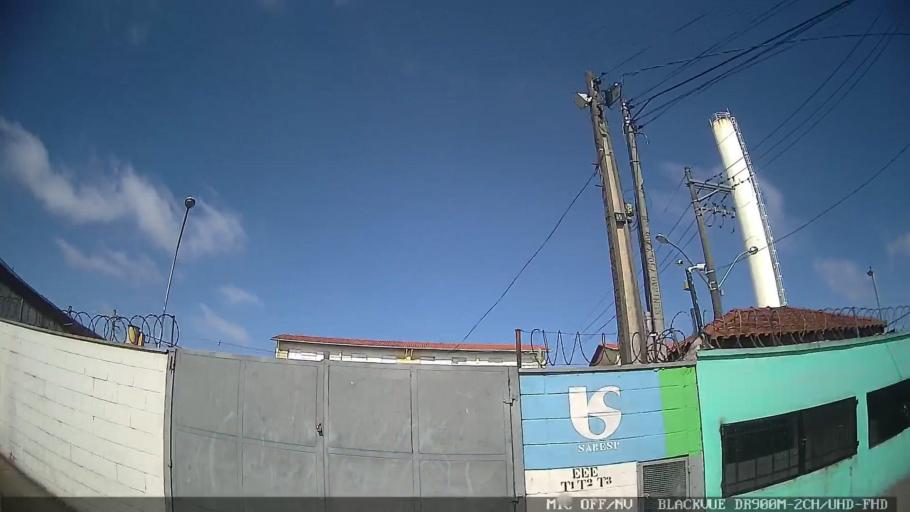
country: BR
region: Sao Paulo
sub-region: Itaquaquecetuba
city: Itaquaquecetuba
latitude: -23.4874
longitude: -46.3415
